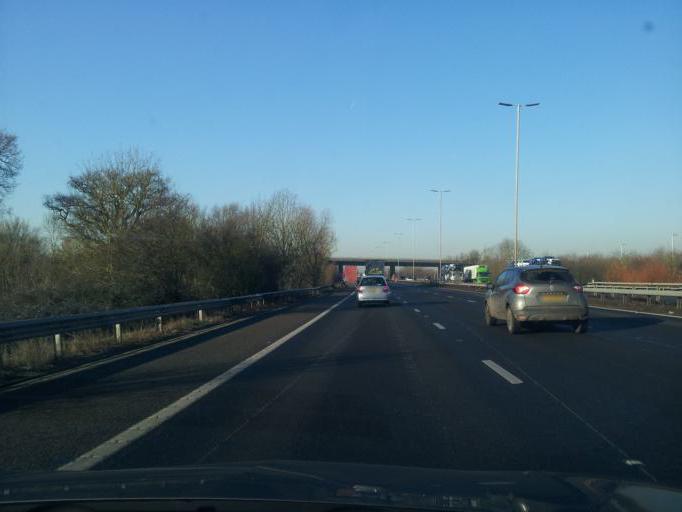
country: GB
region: England
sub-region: Reading
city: Reading
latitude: 51.4188
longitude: -0.9928
